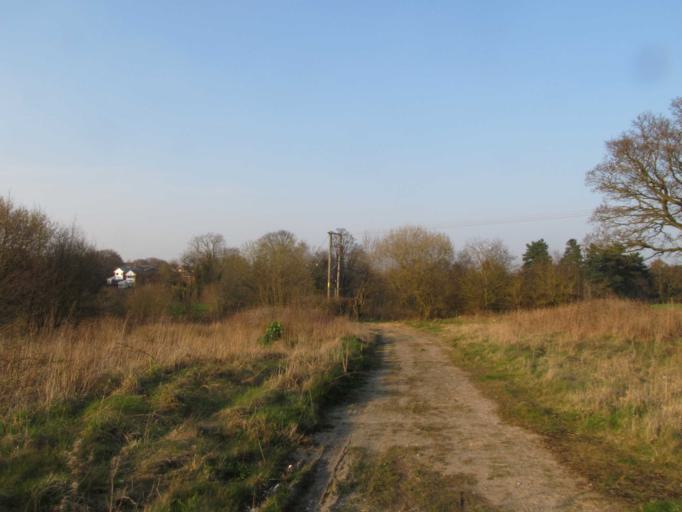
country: GB
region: Wales
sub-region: County of Flintshire
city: Buckley
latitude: 53.1980
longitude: -3.0891
